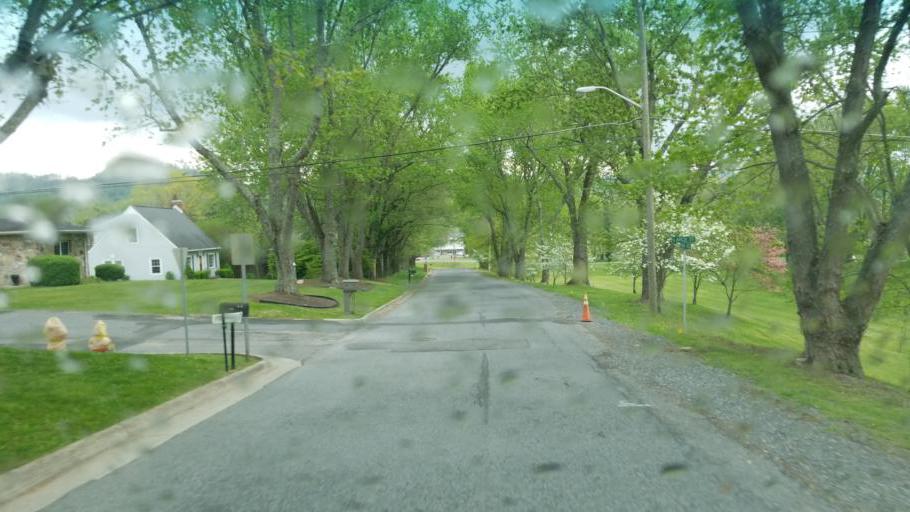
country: US
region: Virginia
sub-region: Smyth County
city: Marion
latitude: 36.8483
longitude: -81.4963
